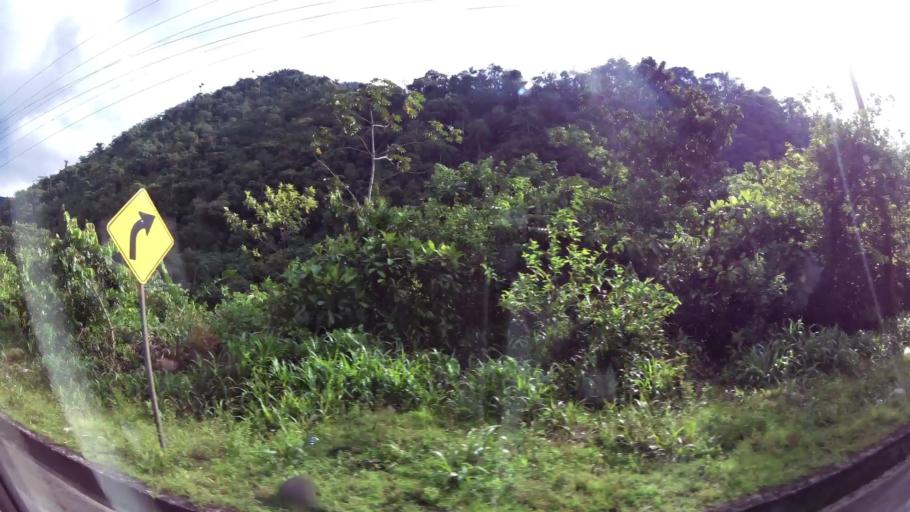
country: EC
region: Pastaza
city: Puyo
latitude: -1.4119
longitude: -78.1865
